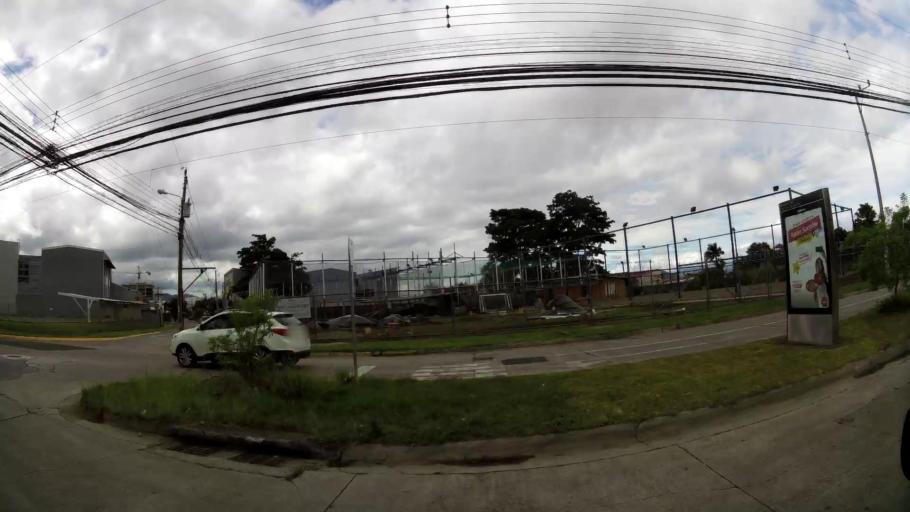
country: CR
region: San Jose
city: San Pedro
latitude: 9.9350
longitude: -84.0580
